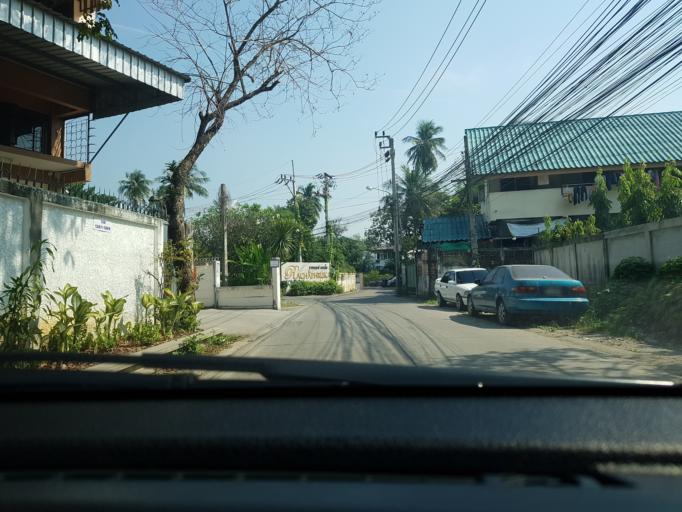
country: TH
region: Bangkok
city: Bangkok Yai
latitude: 13.7302
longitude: 100.4580
